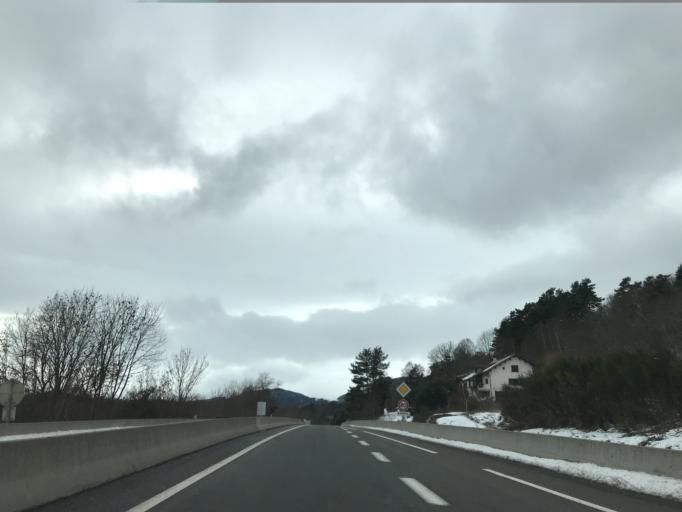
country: FR
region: Auvergne
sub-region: Departement du Puy-de-Dome
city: Saint-Genes-Champanelle
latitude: 45.6939
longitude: 2.9960
